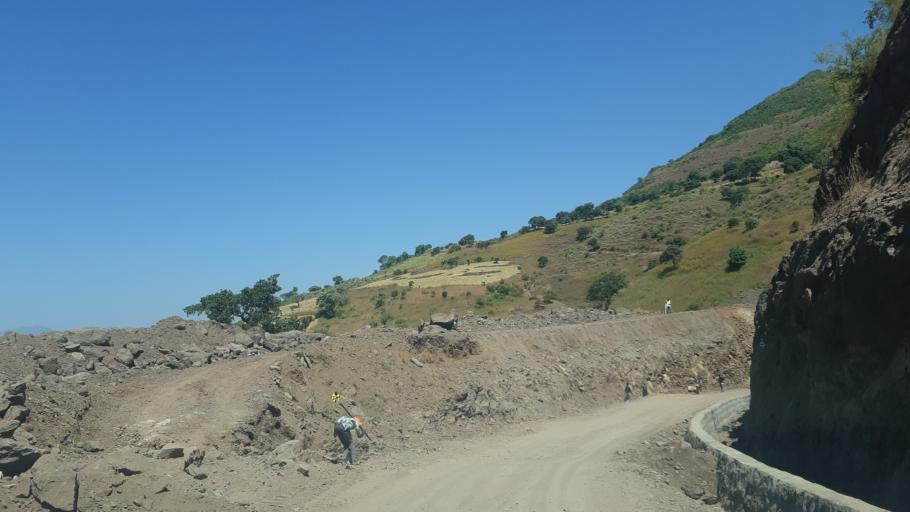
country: ET
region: Amhara
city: Dabat
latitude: 13.1679
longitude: 37.6055
